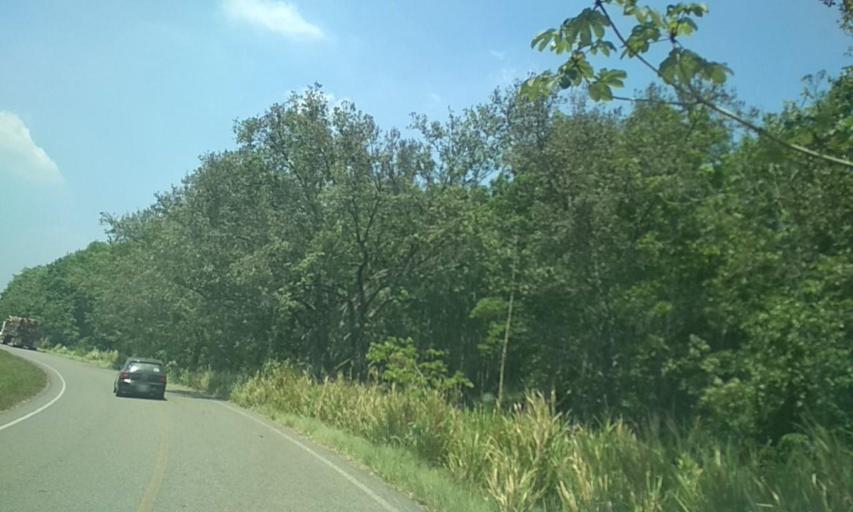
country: MX
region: Tabasco
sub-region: Huimanguillo
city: Paso de la Mina 3ra. Seccion
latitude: 17.8156
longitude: -93.6156
